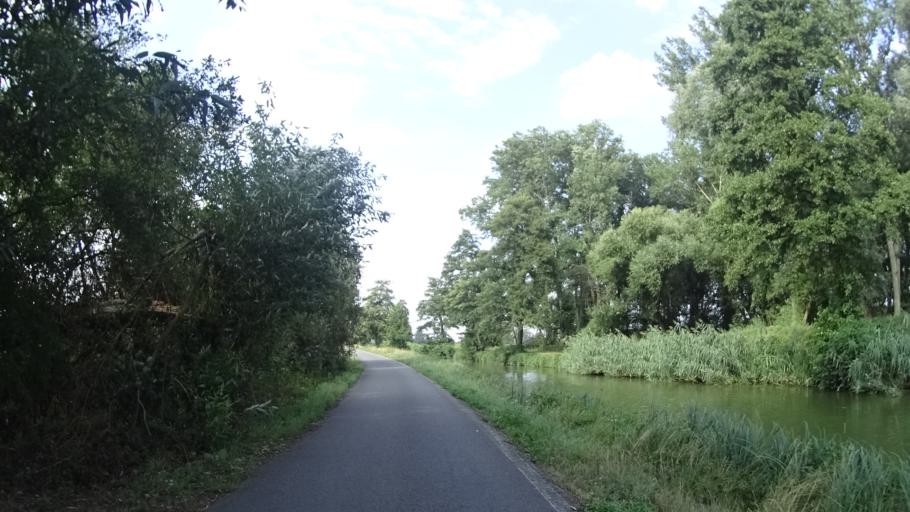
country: CZ
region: Zlin
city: Babice
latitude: 49.1046
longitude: 17.4777
